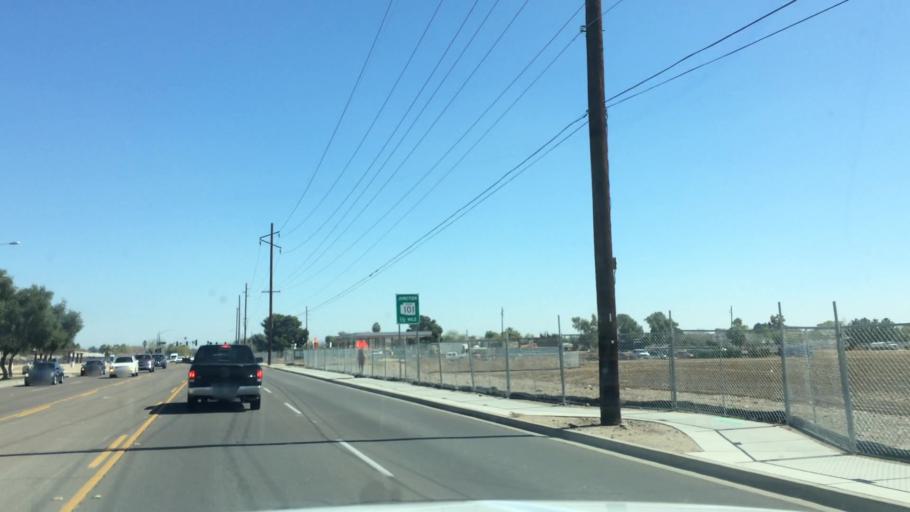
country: US
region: Arizona
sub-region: Maricopa County
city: Sun City
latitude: 33.5659
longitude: -112.2672
